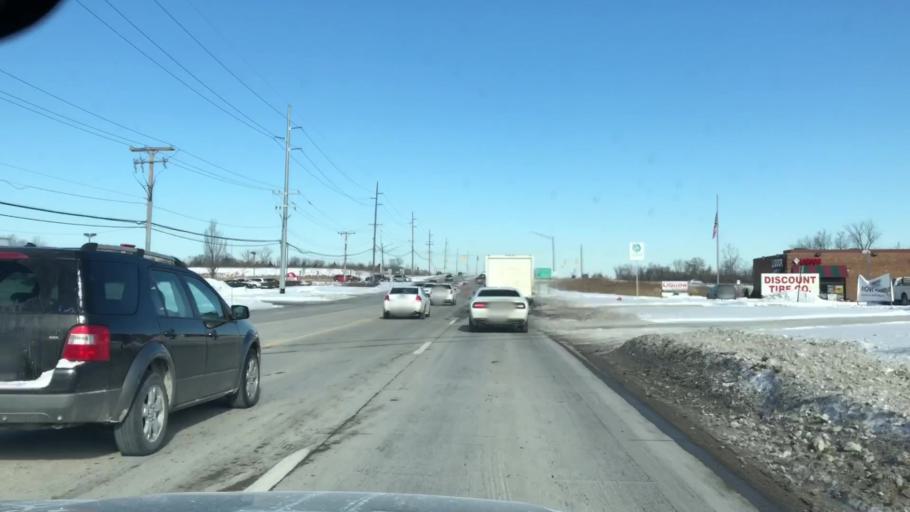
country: US
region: Michigan
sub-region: Oakland County
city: Troy
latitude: 42.6250
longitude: -83.1308
